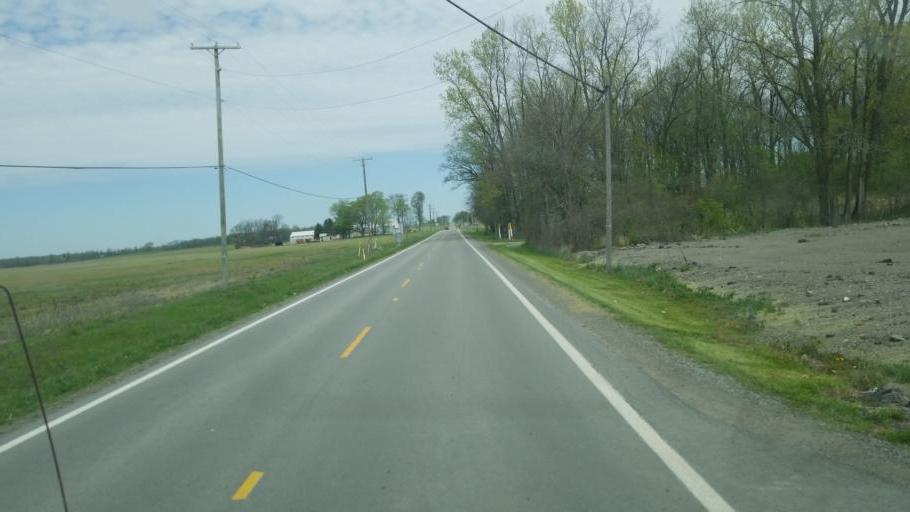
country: US
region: Ohio
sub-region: Hardin County
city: Ada
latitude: 40.6960
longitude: -83.7852
